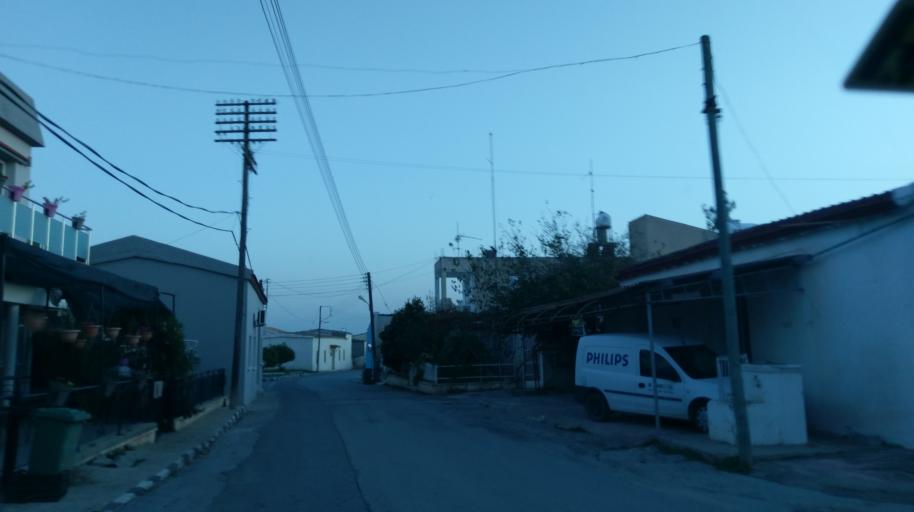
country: CY
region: Ammochostos
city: Trikomo
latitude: 35.2875
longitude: 33.8919
